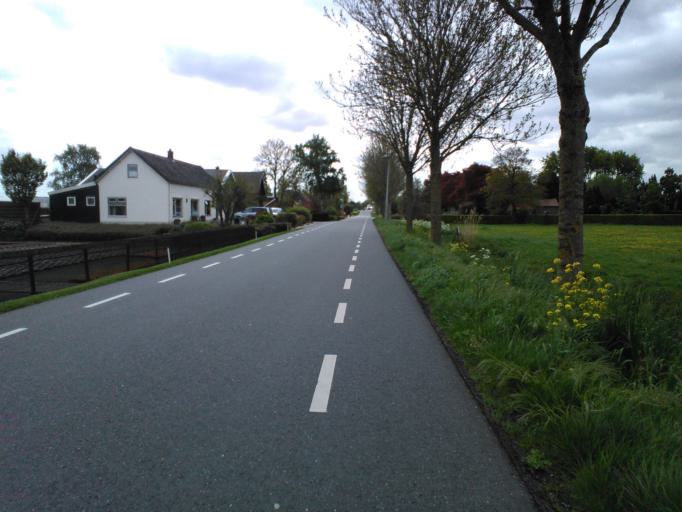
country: NL
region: South Holland
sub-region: Bodegraven-Reeuwijk
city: Reeuwijk
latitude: 52.0631
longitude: 4.7098
